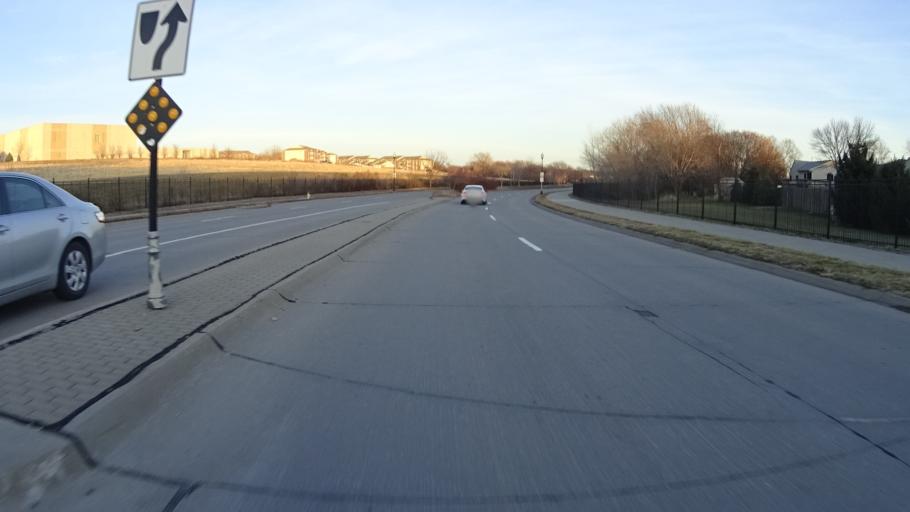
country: US
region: Nebraska
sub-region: Sarpy County
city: Papillion
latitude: 41.1327
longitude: -96.0409
